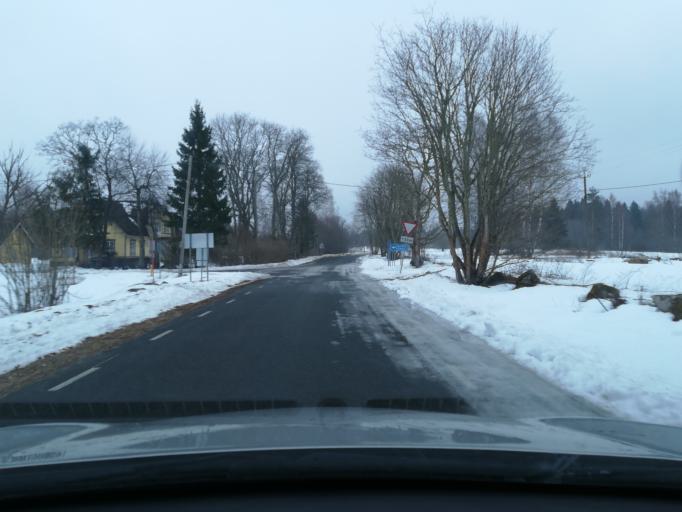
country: EE
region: Harju
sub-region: Loksa linn
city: Loksa
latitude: 59.4658
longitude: 25.7036
